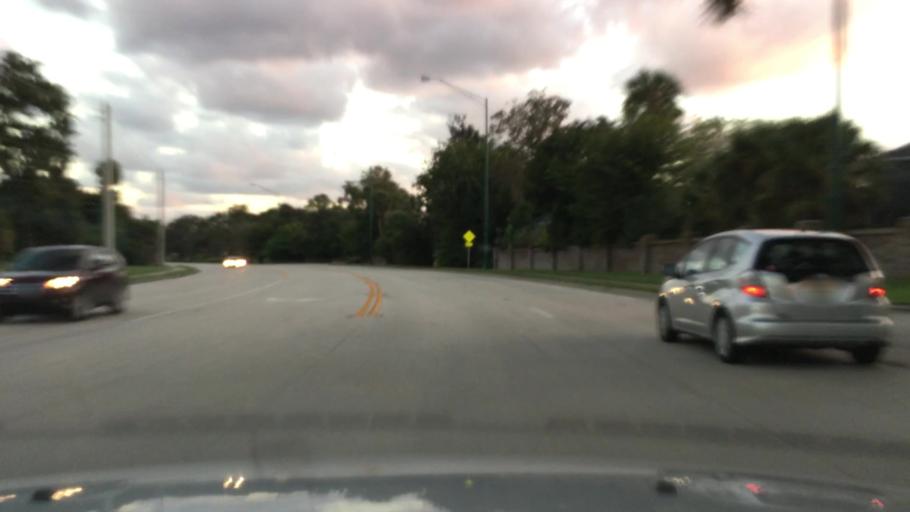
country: US
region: Florida
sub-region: Volusia County
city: Ormond Beach
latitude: 29.2941
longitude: -81.0878
